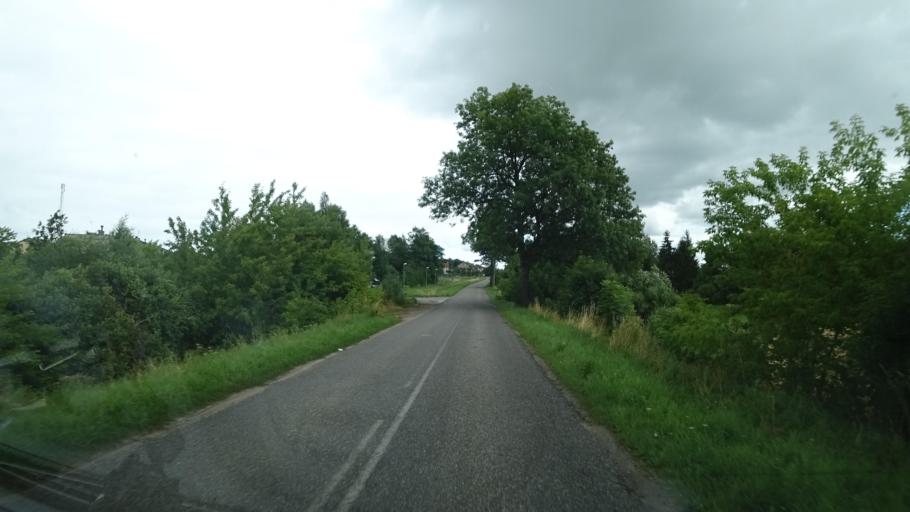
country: PL
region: Warmian-Masurian Voivodeship
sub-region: Powiat goldapski
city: Goldap
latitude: 54.3058
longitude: 22.4195
